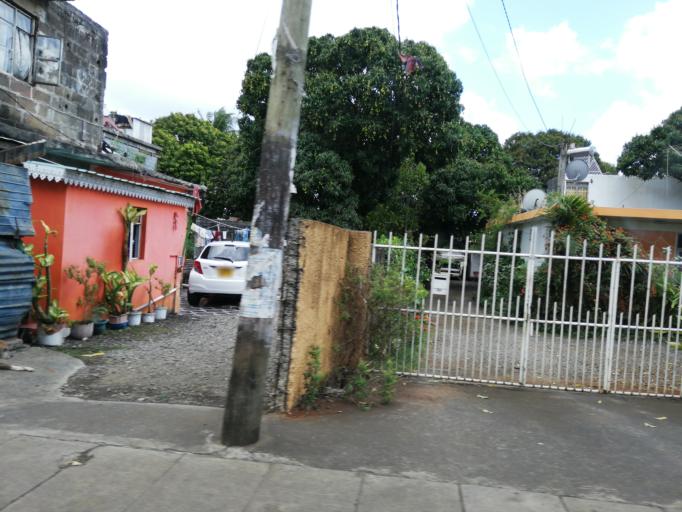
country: MU
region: Pamplemousses
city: Triolet
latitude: -20.0568
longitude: 57.5523
